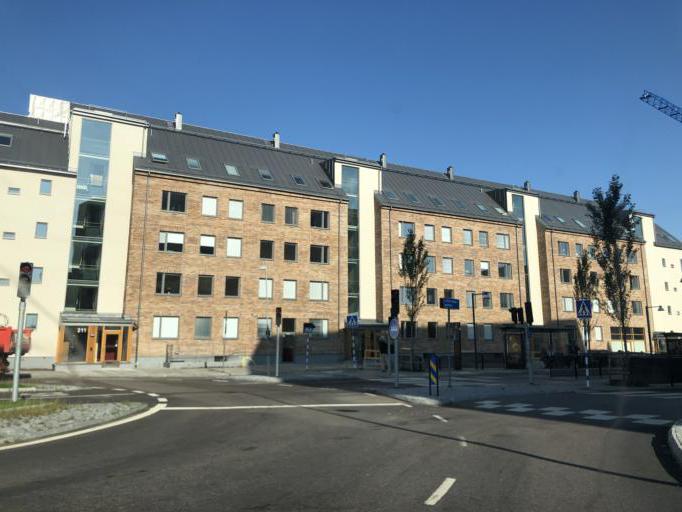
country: SE
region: Vaestra Goetaland
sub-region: Goteborg
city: Goeteborg
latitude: 57.7494
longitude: 11.9810
